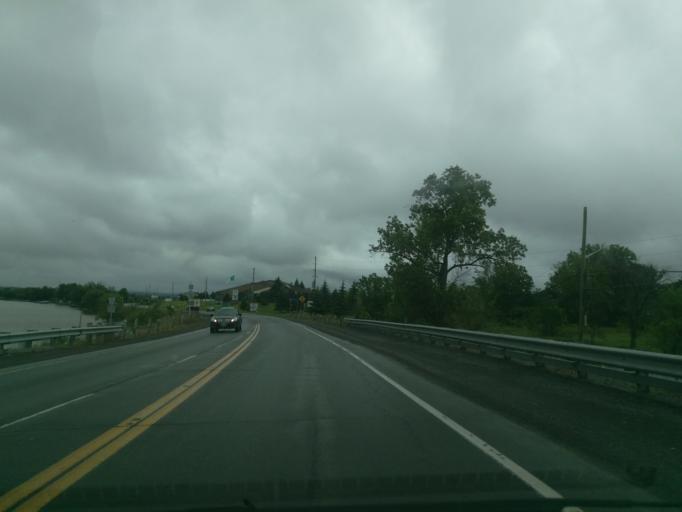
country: CA
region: Ontario
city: Clarence-Rockland
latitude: 45.5359
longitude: -75.3066
